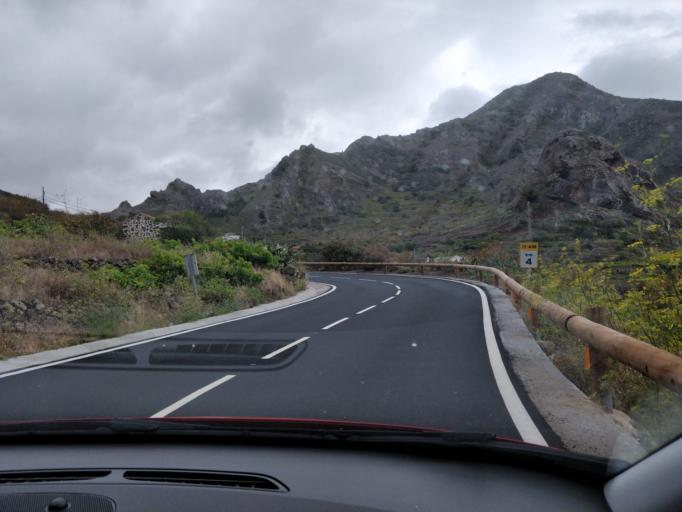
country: ES
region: Canary Islands
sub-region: Provincia de Santa Cruz de Tenerife
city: Tanque
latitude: 28.3528
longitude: -16.8448
